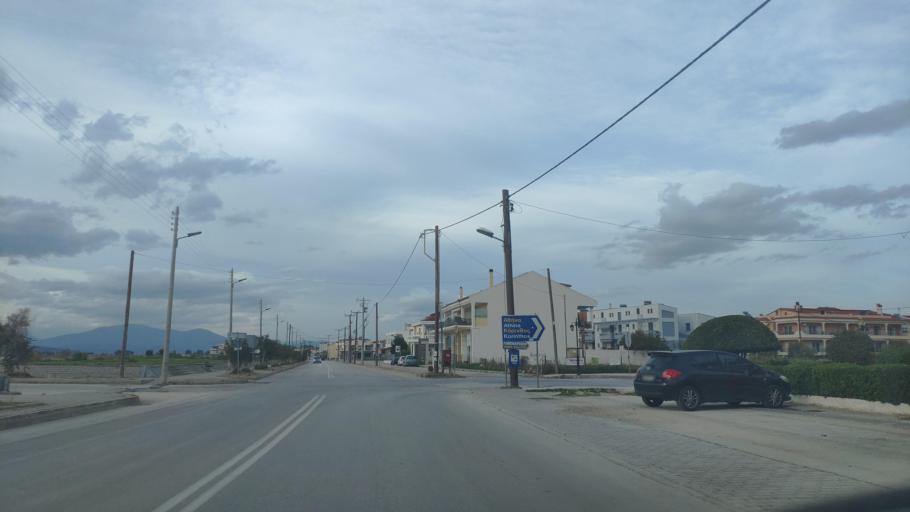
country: GR
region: Peloponnese
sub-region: Nomos Argolidos
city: Nafplio
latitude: 37.5728
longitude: 22.8026
